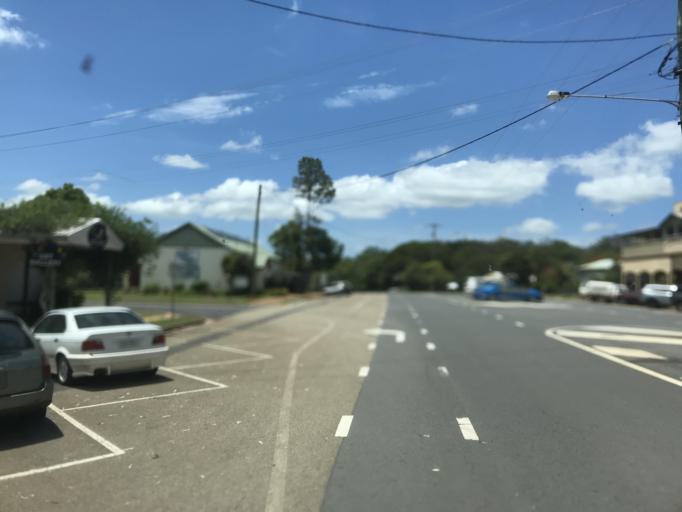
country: AU
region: Queensland
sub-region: Tablelands
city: Ravenshoe
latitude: -17.6054
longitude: 145.4819
